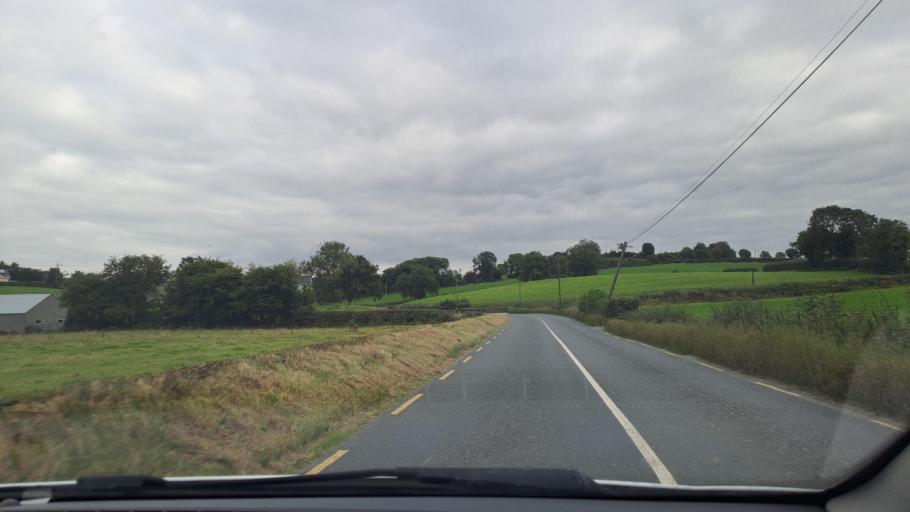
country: IE
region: Ulster
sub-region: An Cabhan
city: Kingscourt
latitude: 53.9964
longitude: -6.8262
